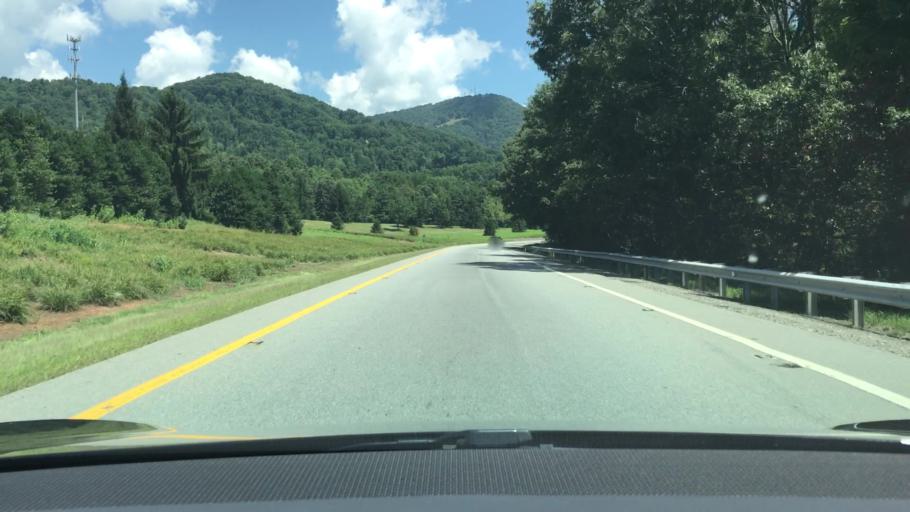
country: US
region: North Carolina
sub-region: Haywood County
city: Clyde
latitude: 35.5402
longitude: -82.9175
